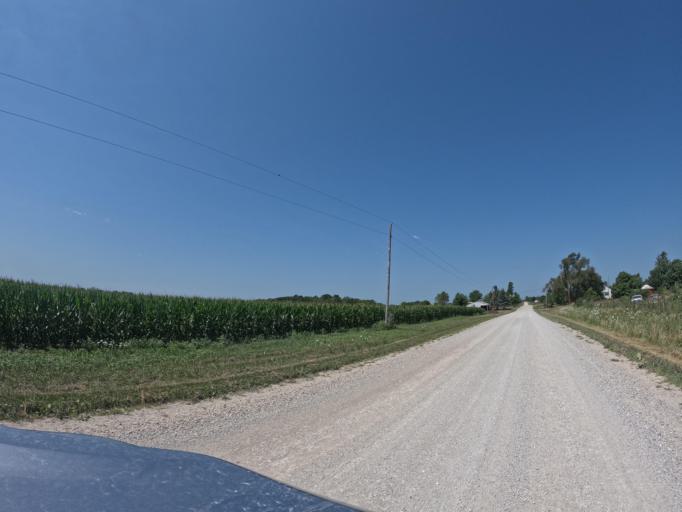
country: US
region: Iowa
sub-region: Henry County
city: Mount Pleasant
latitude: 40.8892
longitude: -91.5808
